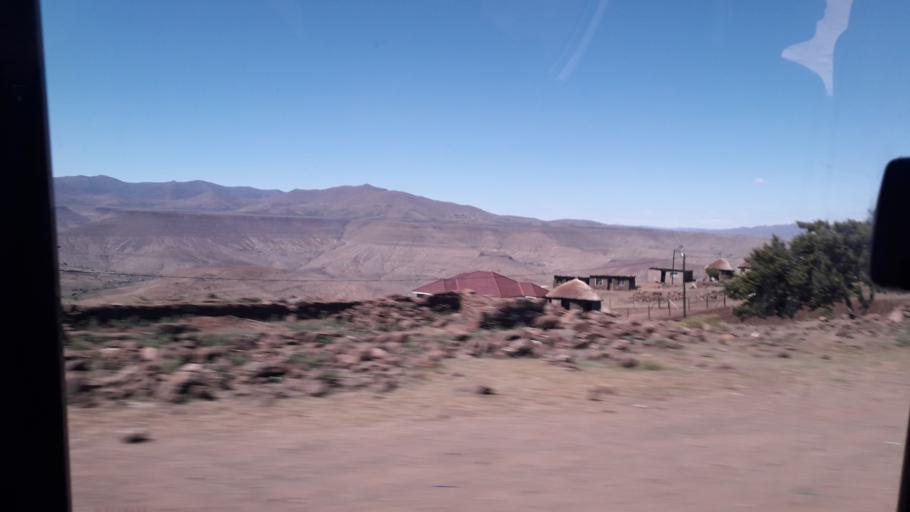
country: LS
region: Mokhotlong
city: Mokhotlong
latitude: -29.2783
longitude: 28.9366
